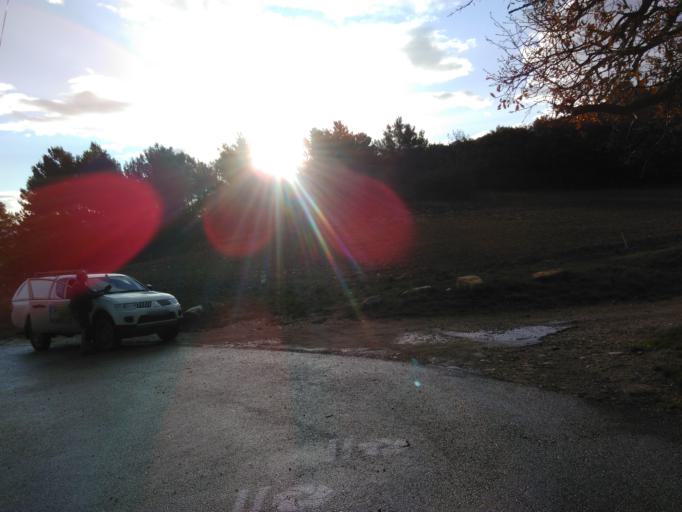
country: FR
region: Provence-Alpes-Cote d'Azur
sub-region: Departement du Vaucluse
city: Malaucene
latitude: 44.1794
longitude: 5.0965
